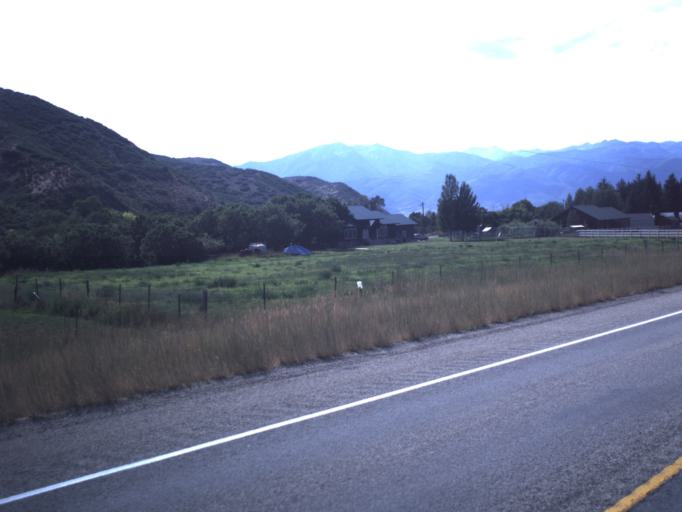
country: US
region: Utah
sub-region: Wasatch County
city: Heber
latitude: 40.4555
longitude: -111.3751
